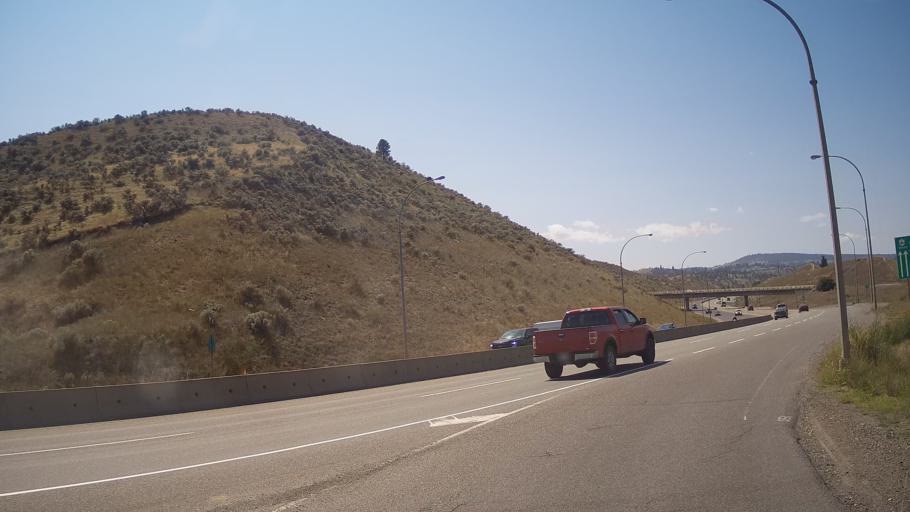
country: CA
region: British Columbia
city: Kamloops
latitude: 50.6719
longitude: -120.2997
